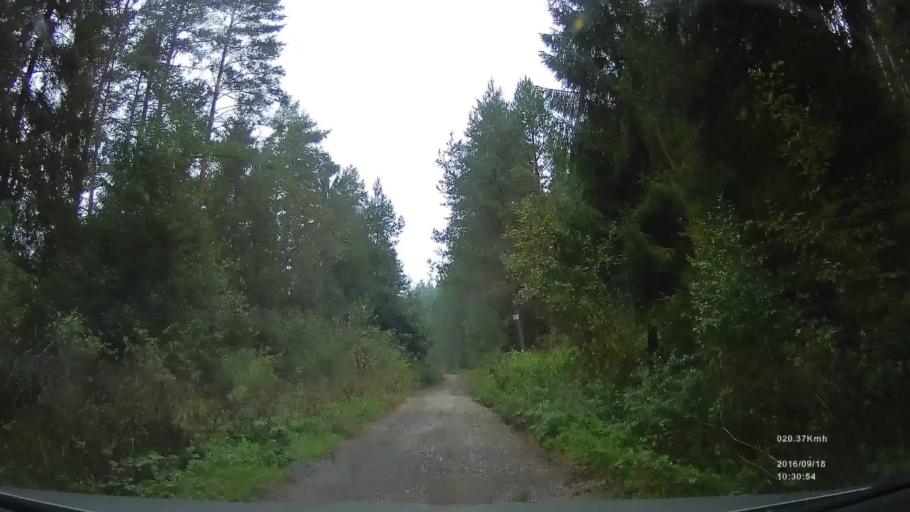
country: SK
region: Kosicky
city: Spisska Nova Ves
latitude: 48.9595
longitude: 20.6235
